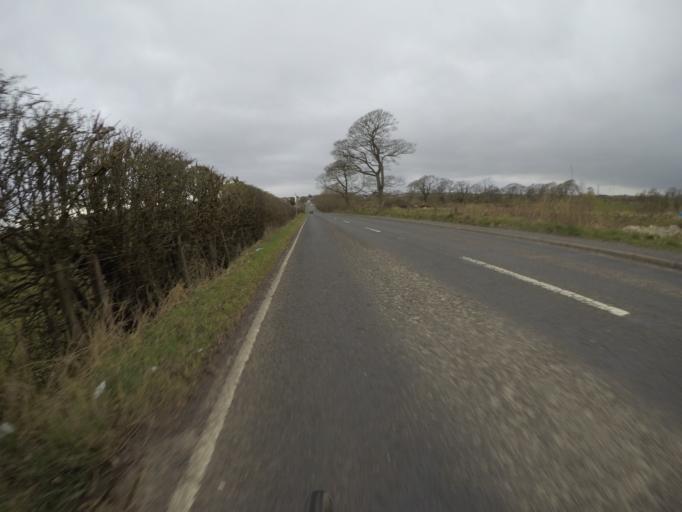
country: GB
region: Scotland
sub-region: North Ayrshire
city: Springside
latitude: 55.6122
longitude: -4.5797
